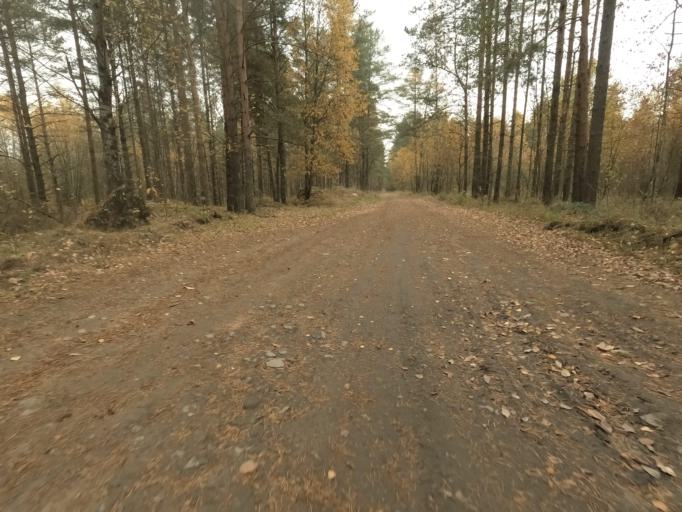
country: RU
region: Leningrad
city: Kirovsk
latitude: 59.8501
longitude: 30.9758
